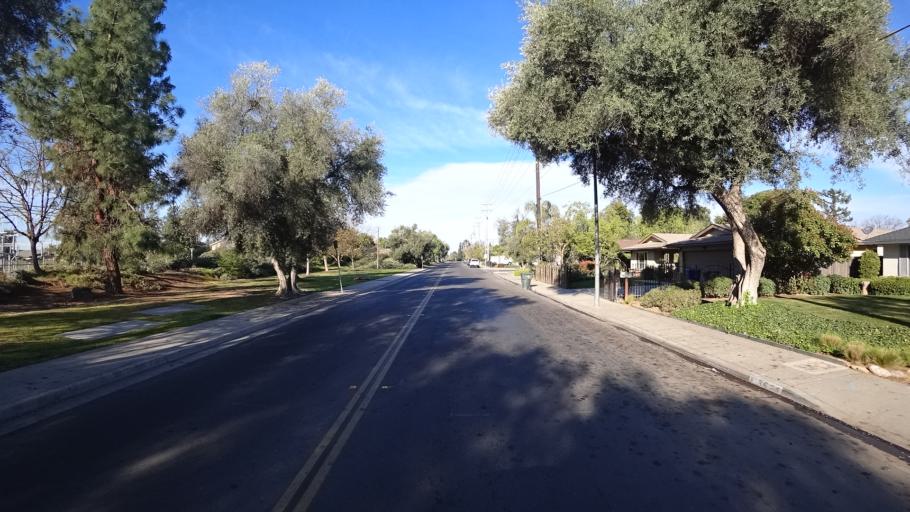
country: US
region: California
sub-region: Fresno County
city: West Park
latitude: 36.8227
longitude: -119.8586
